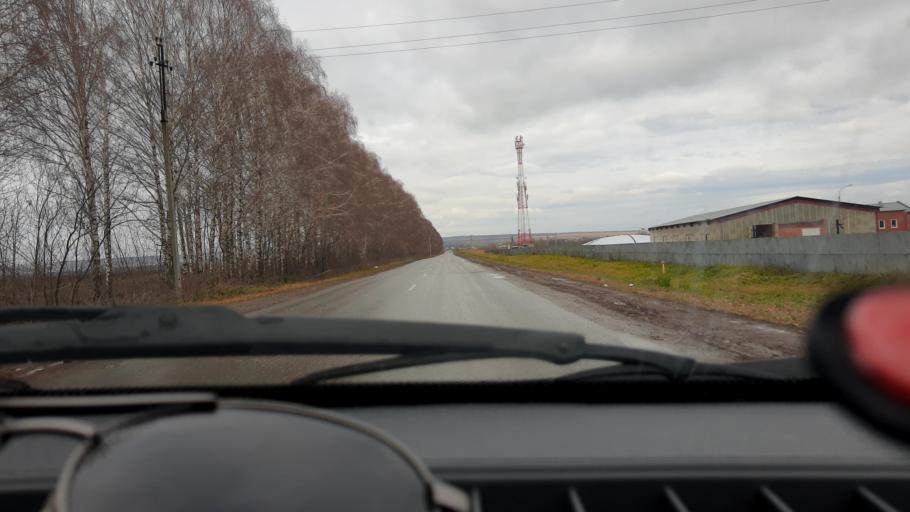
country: RU
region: Bashkortostan
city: Ufa
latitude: 54.8245
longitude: 55.9852
